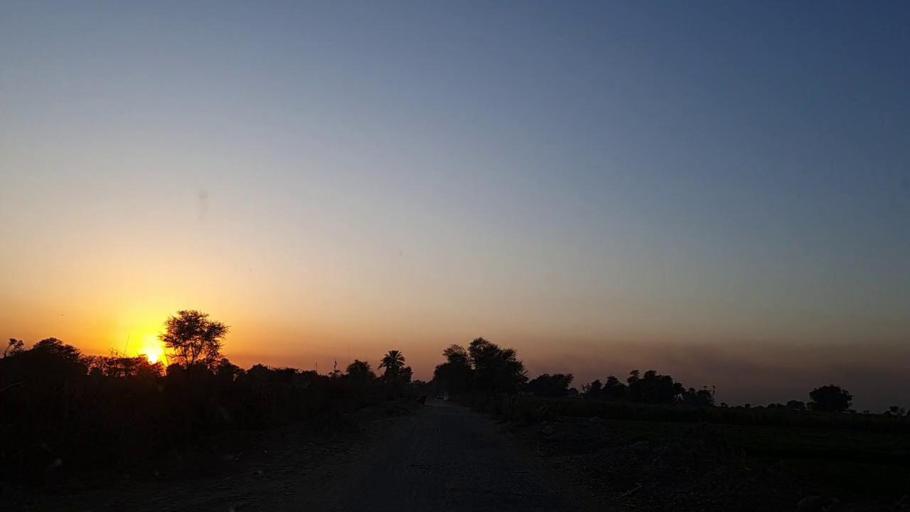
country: PK
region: Sindh
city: Daur
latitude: 26.3426
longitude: 68.2901
